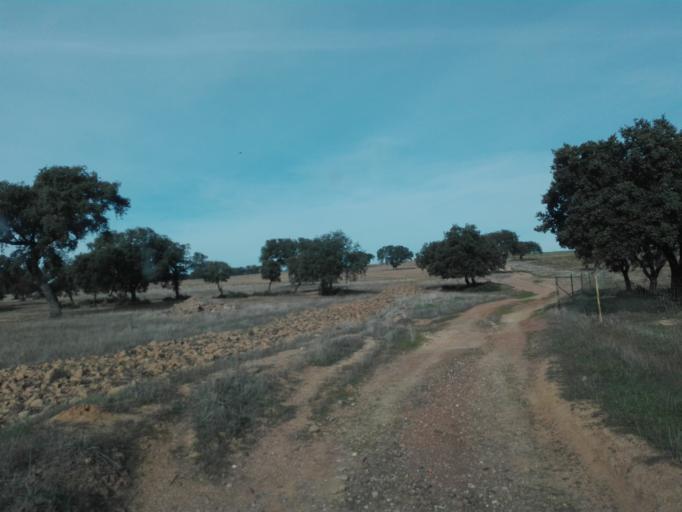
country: ES
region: Extremadura
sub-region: Provincia de Badajoz
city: Campillo de Llerena
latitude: 38.4699
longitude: -5.8898
